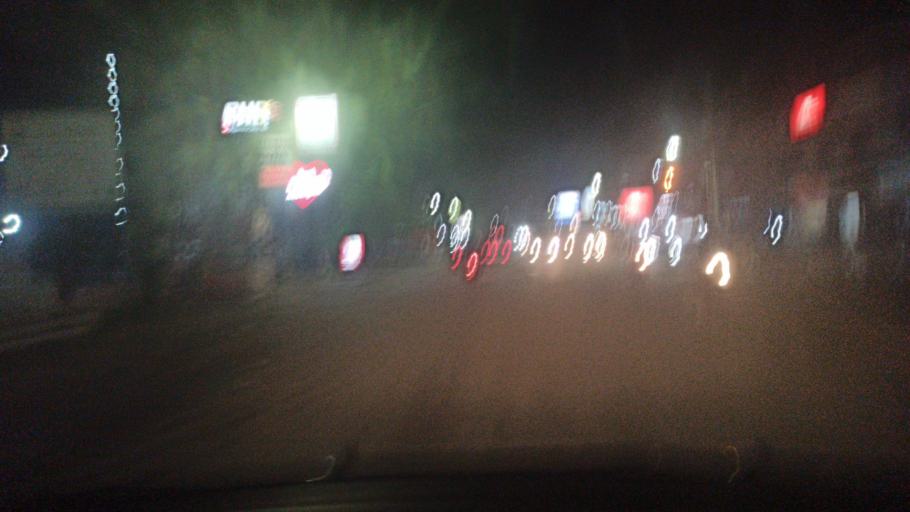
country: ID
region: South Sumatra
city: Plaju
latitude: -2.9483
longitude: 104.7855
